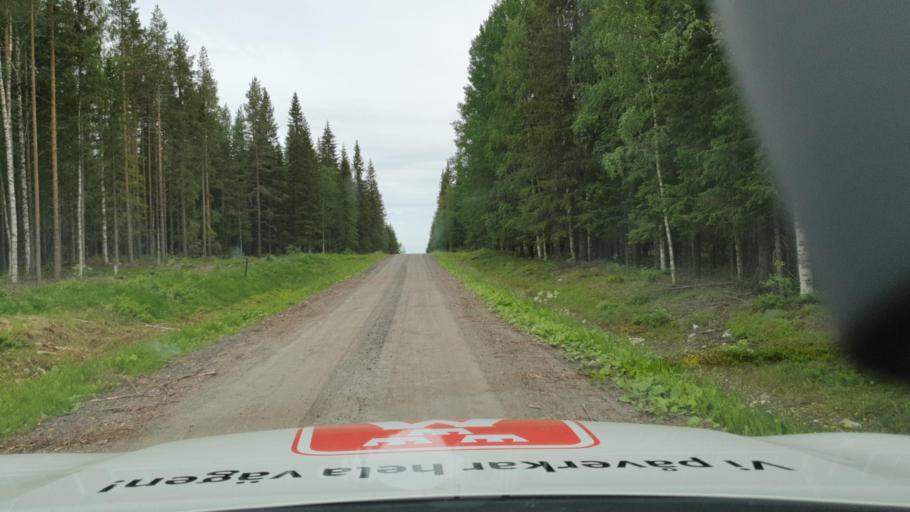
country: SE
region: Vaesterbotten
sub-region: Skelleftea Kommun
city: Burtraesk
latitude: 64.3764
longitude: 20.6153
